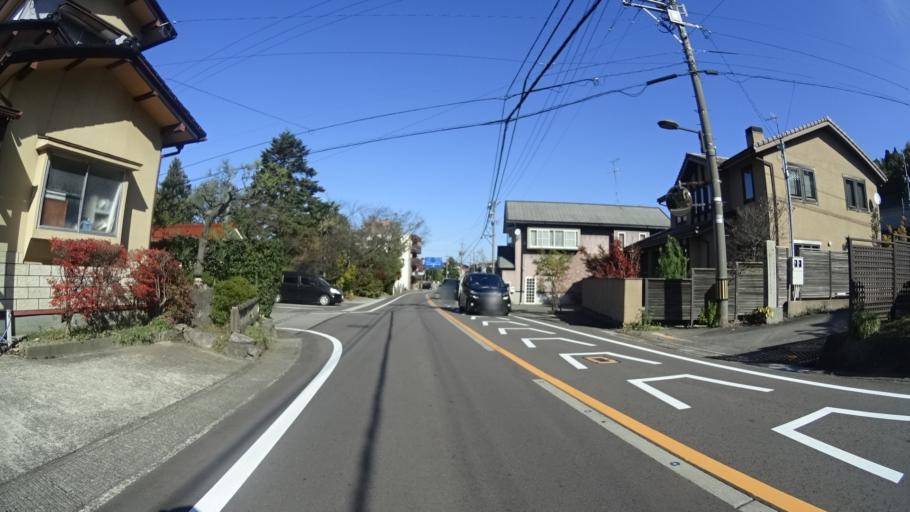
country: JP
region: Ishikawa
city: Nonoichi
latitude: 36.5006
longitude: 136.6226
